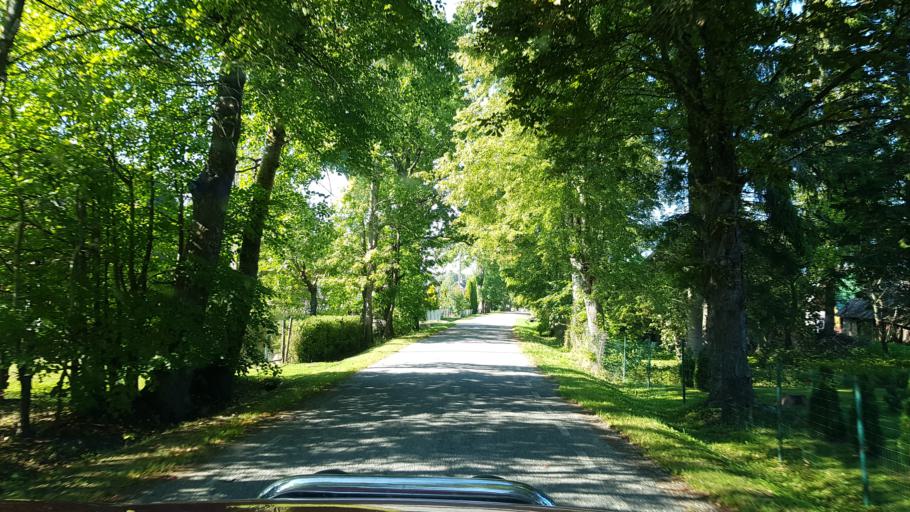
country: EE
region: Polvamaa
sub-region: Raepina vald
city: Rapina
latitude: 58.2337
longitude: 27.4732
